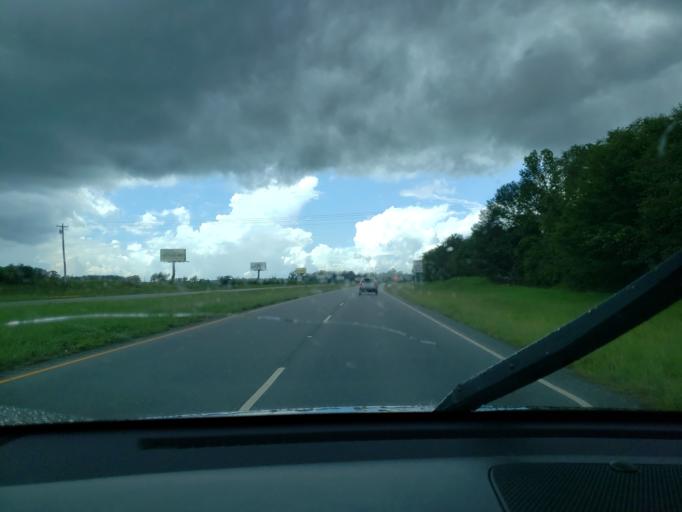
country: US
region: North Carolina
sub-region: Bladen County
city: Elizabethtown
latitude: 34.6043
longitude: -78.6228
